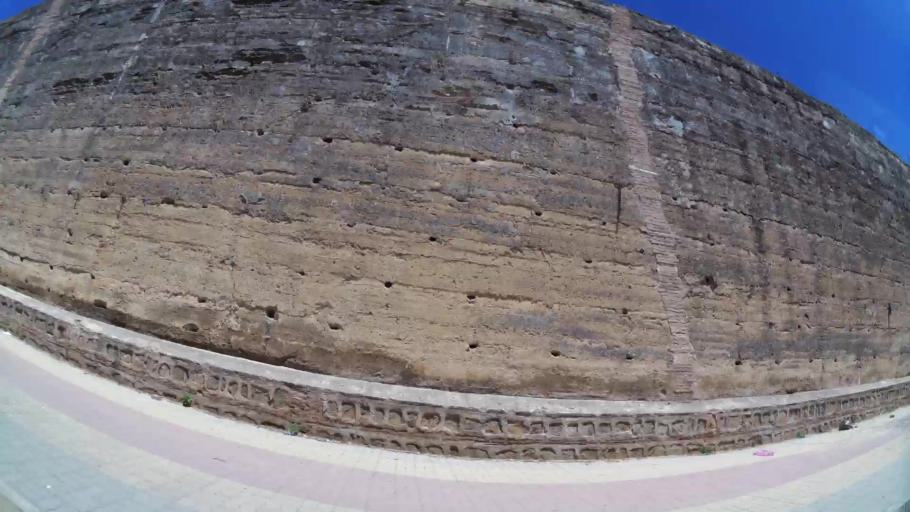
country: MA
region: Meknes-Tafilalet
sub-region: Meknes
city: Meknes
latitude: 33.9073
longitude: -5.5752
